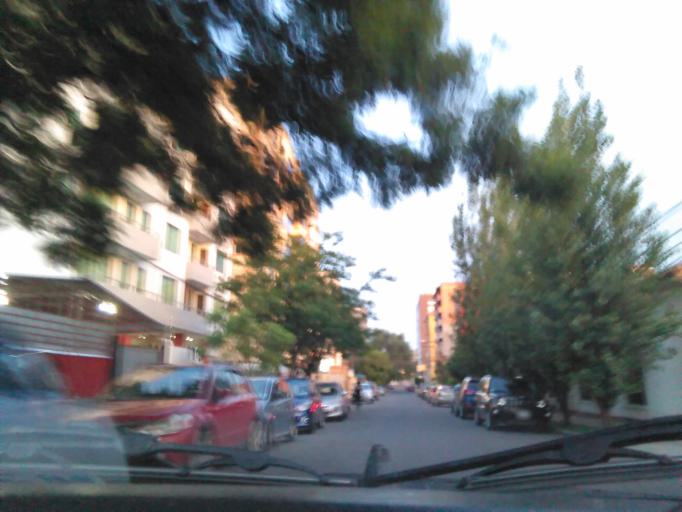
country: BO
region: Cochabamba
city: Cochabamba
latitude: -17.3682
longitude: -66.1672
